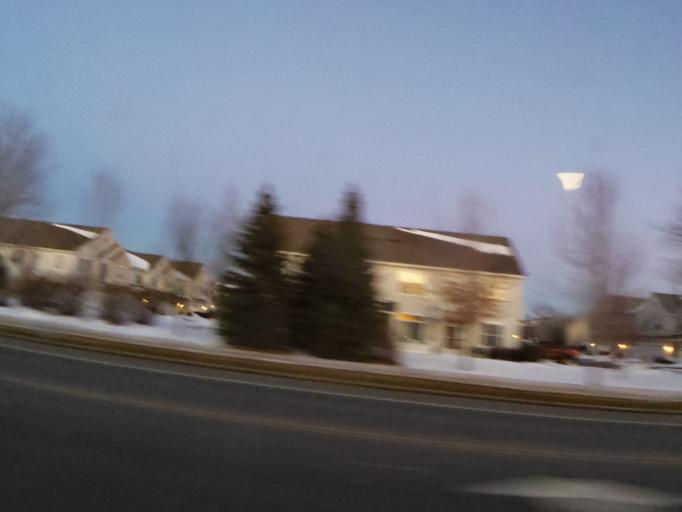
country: US
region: Minnesota
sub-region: Scott County
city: Shakopee
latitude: 44.7734
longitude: -93.5202
